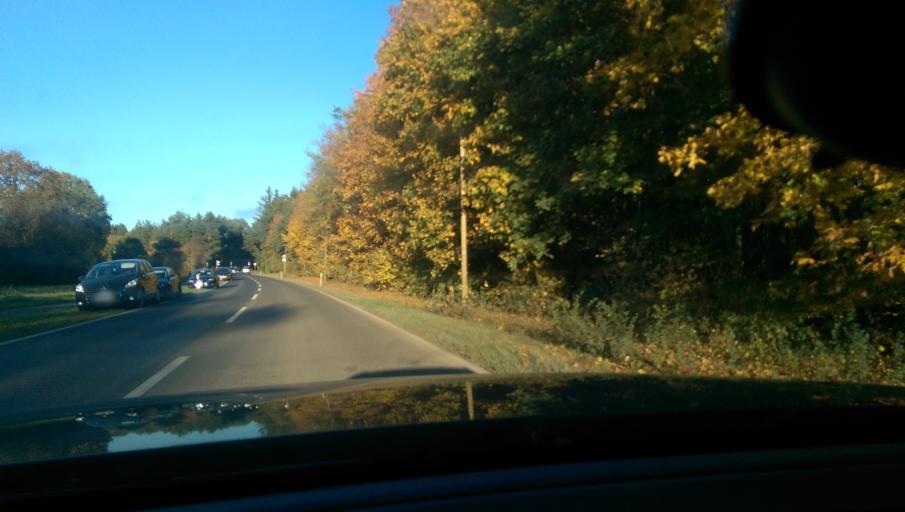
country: DE
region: Bavaria
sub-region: Regierungsbezirk Unterfranken
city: Schwebheim
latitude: 50.0123
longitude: 10.2287
